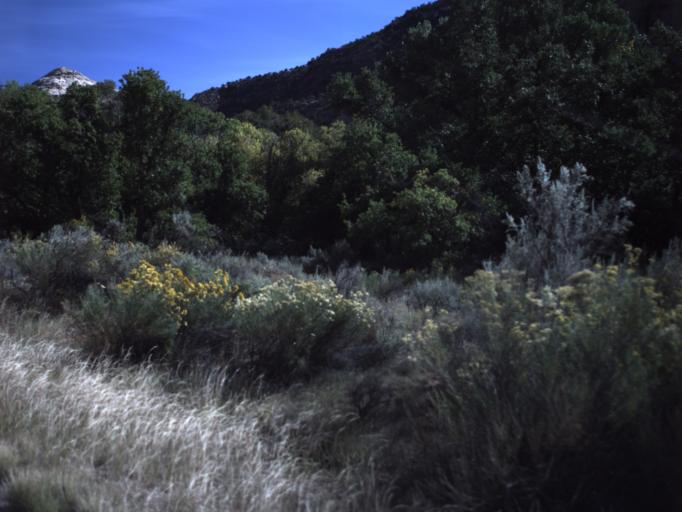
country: US
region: Utah
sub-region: San Juan County
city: Monticello
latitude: 38.0013
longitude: -109.5317
